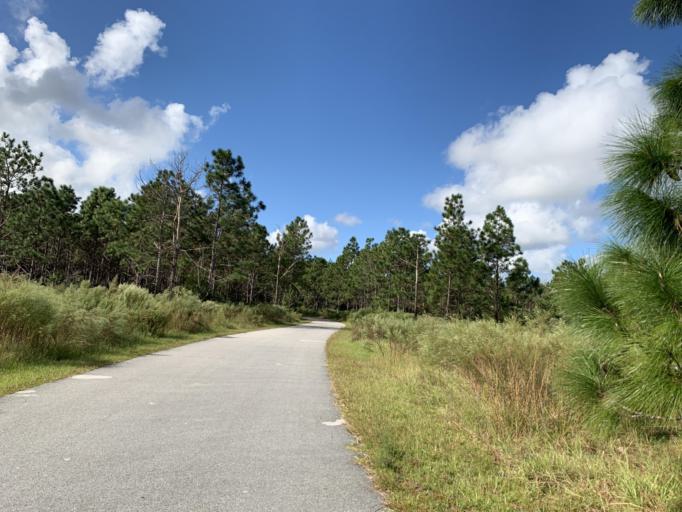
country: US
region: Florida
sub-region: Marion County
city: Silver Springs Shores
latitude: 29.1546
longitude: -82.0416
